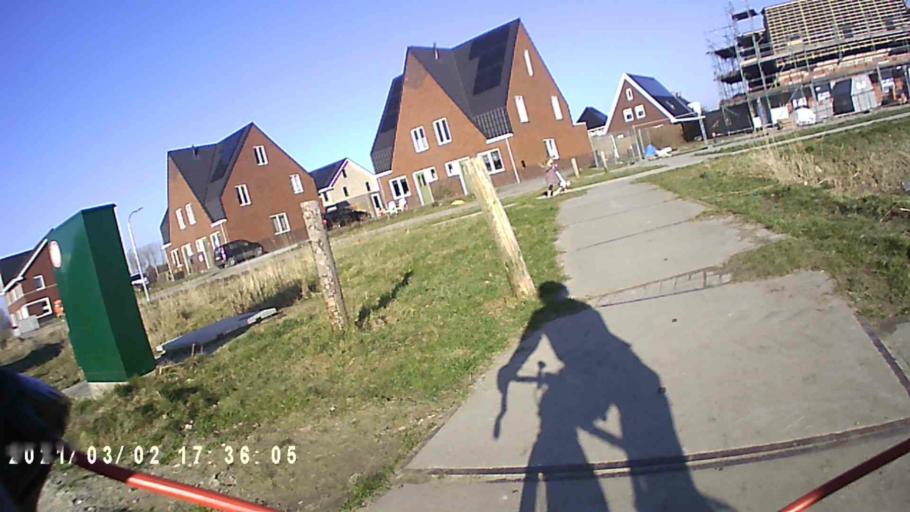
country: NL
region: Groningen
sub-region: Gemeente Zuidhorn
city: Zuidhorn
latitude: 53.2523
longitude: 6.4115
